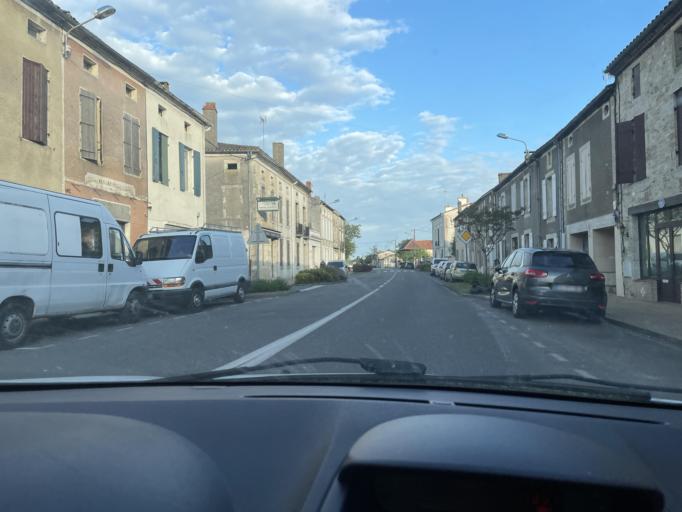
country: FR
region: Aquitaine
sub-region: Departement de la Gironde
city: Grignols
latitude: 44.3870
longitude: -0.0439
